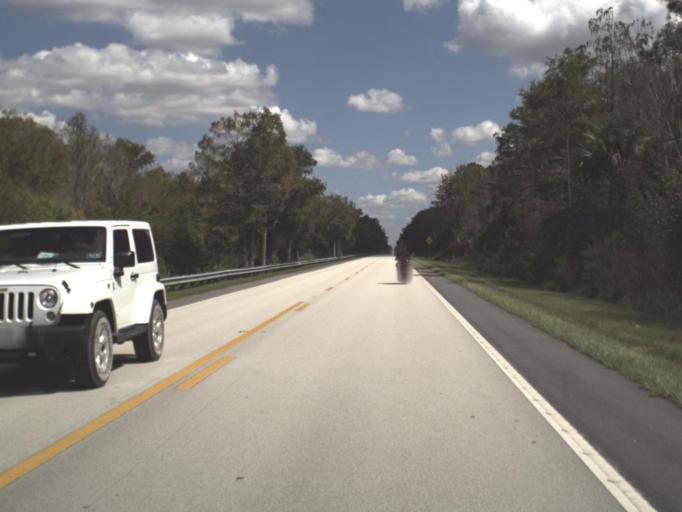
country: US
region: Florida
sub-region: Collier County
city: Marco
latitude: 25.8774
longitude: -81.2350
